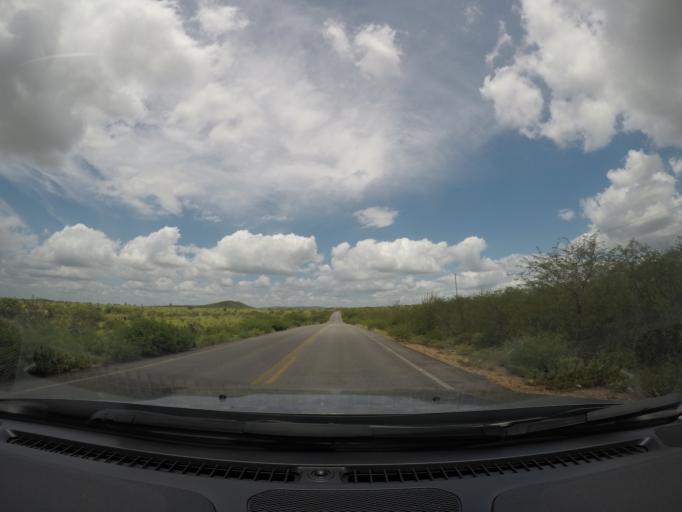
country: BR
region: Bahia
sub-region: Ipira
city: Ipira
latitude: -12.2441
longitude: -39.8054
